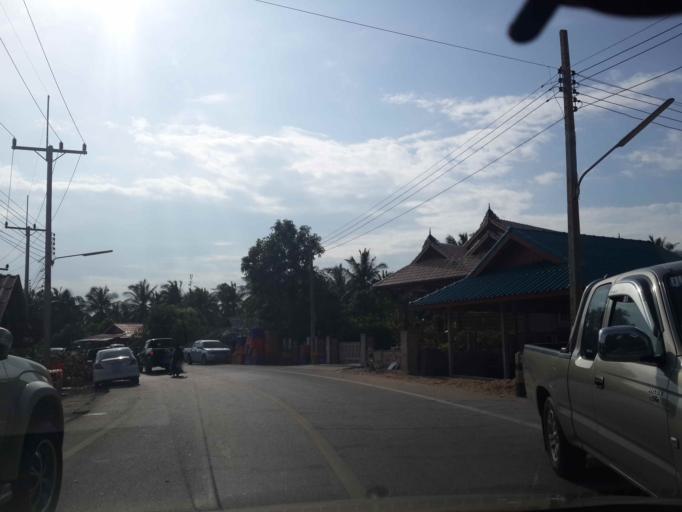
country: TH
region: Pattani
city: Yaring
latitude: 6.9291
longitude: 101.3221
